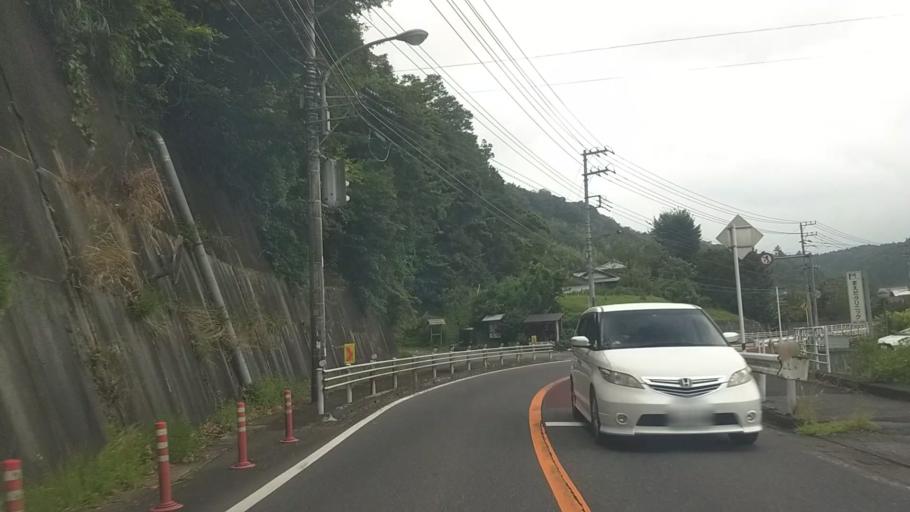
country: JP
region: Chiba
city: Kisarazu
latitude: 35.2918
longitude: 140.0831
